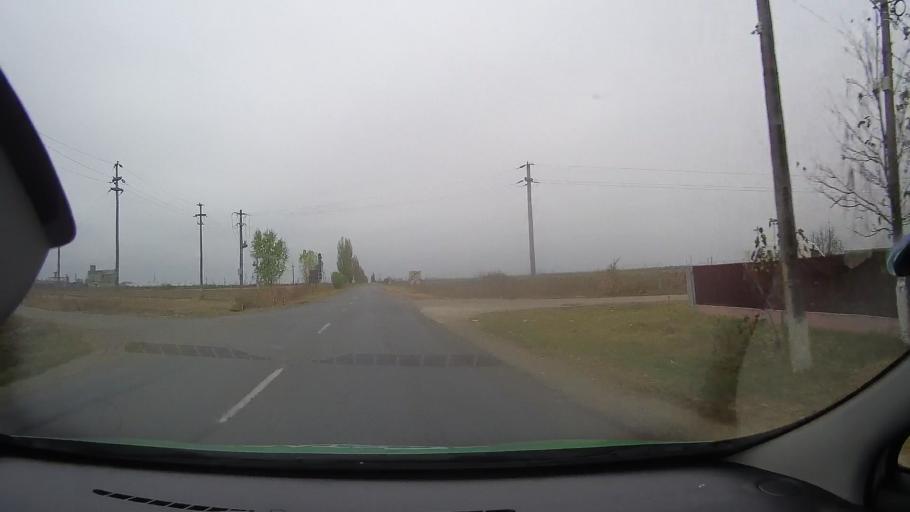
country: RO
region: Ialomita
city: Tandarei
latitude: 44.6557
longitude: 27.6528
